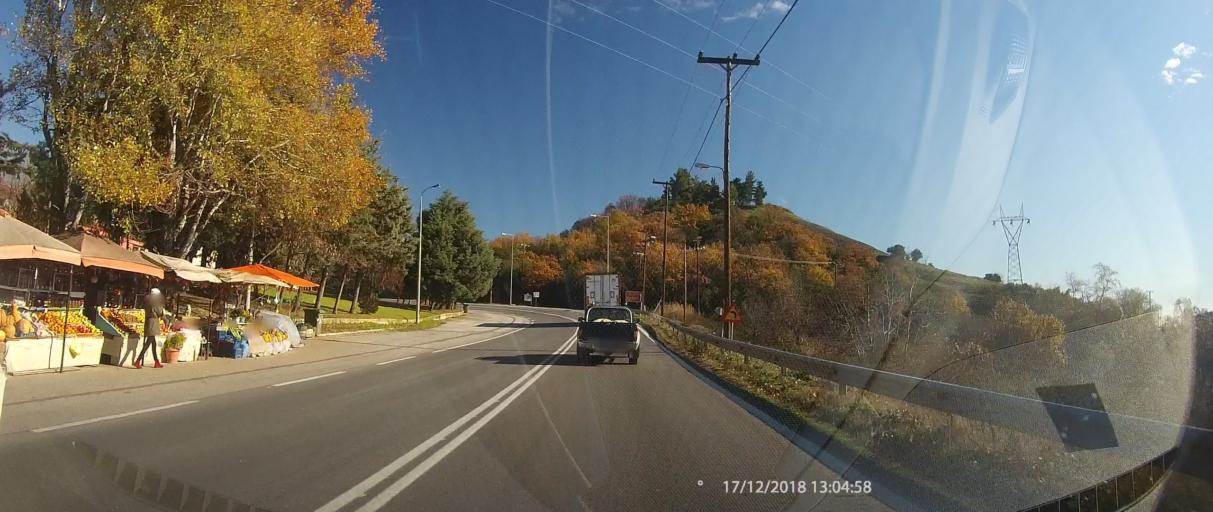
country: GR
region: Thessaly
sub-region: Trikala
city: Kalampaka
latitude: 39.7028
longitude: 21.6153
